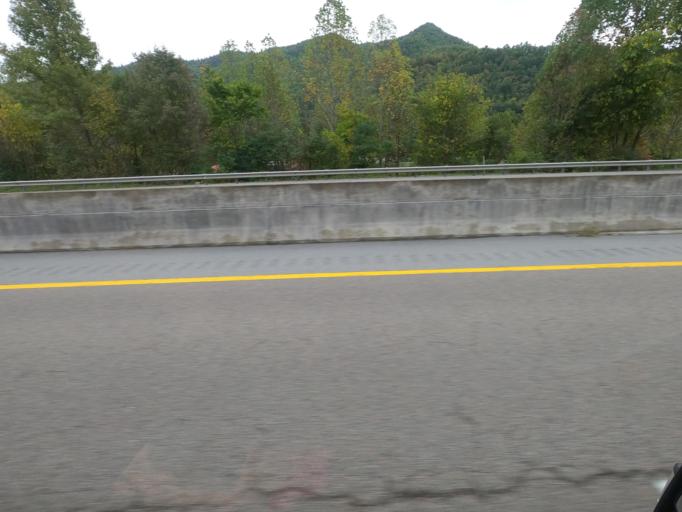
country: US
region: Tennessee
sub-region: Unicoi County
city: Banner Hill
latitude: 36.0918
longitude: -82.4850
